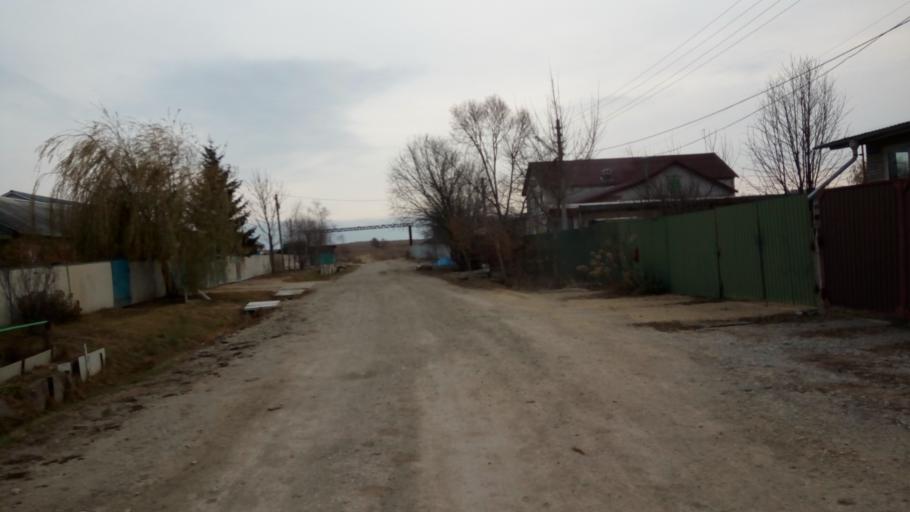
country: RU
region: Primorskiy
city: Novoshakhtinskiy
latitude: 44.0233
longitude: 132.1777
